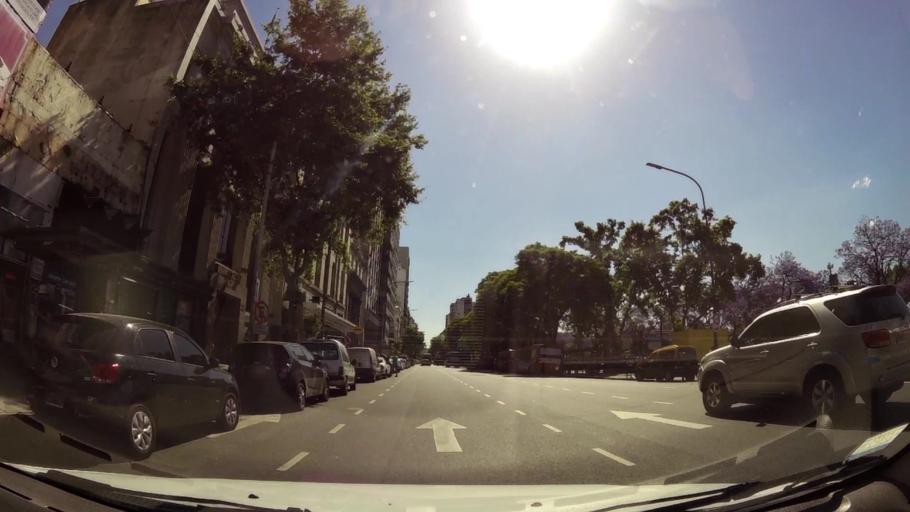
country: AR
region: Buenos Aires F.D.
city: Buenos Aires
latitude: -34.6102
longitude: -58.4063
